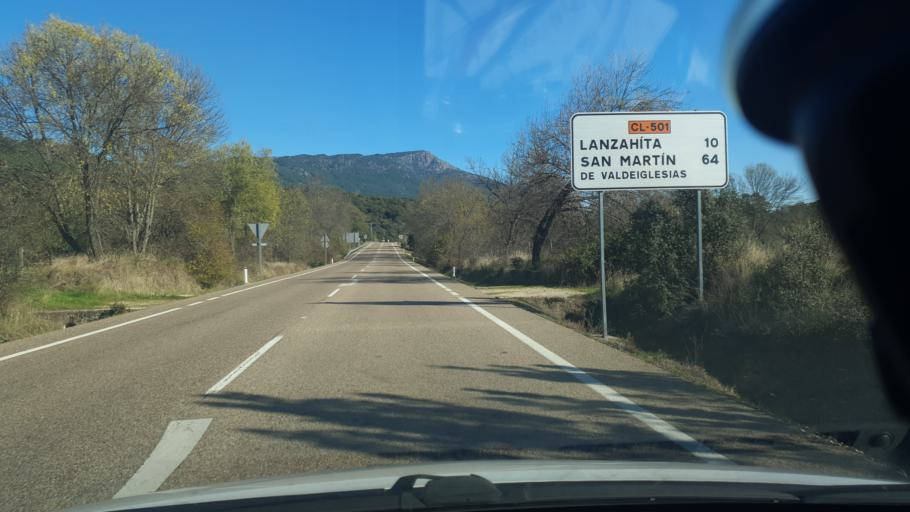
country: ES
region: Castille and Leon
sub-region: Provincia de Avila
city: Arenas de San Pedro
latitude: 40.1809
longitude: -5.0386
